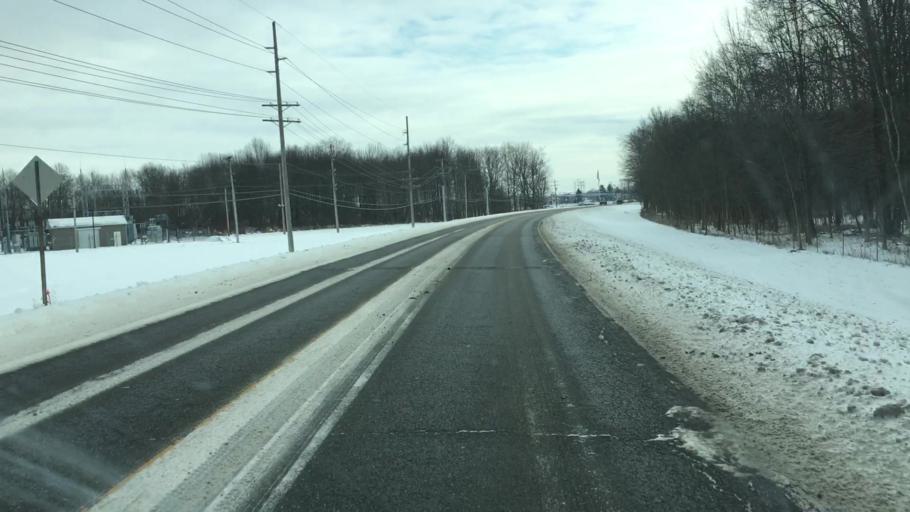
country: US
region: Ohio
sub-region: Columbiana County
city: Columbiana
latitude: 40.8984
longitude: -80.6839
